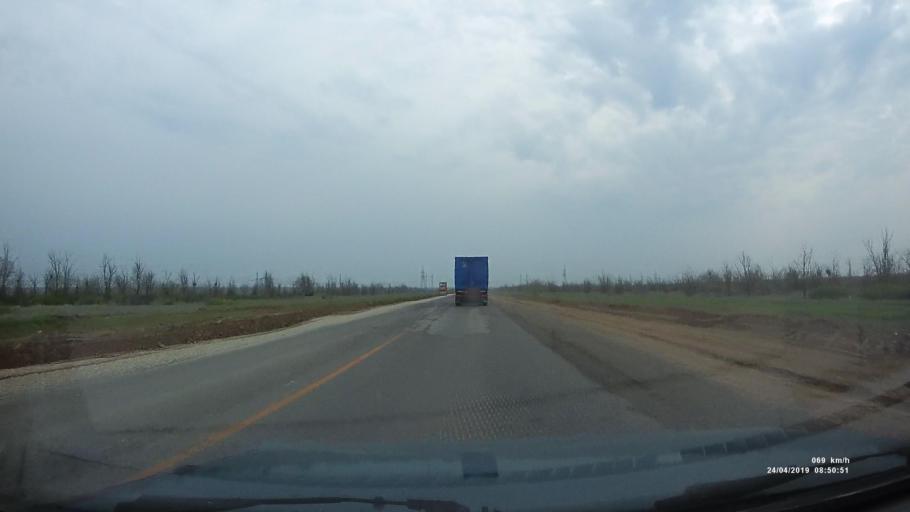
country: RU
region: Kalmykiya
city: Arshan'
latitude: 46.2640
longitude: 44.1425
